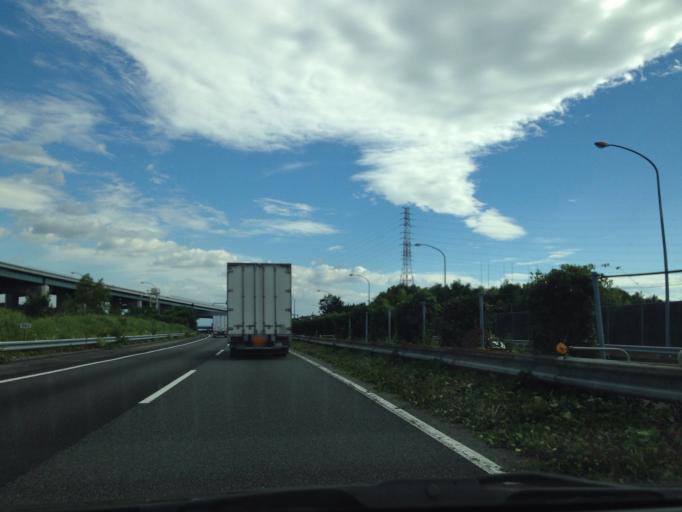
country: JP
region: Shizuoka
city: Gotemba
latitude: 35.2559
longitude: 138.9094
